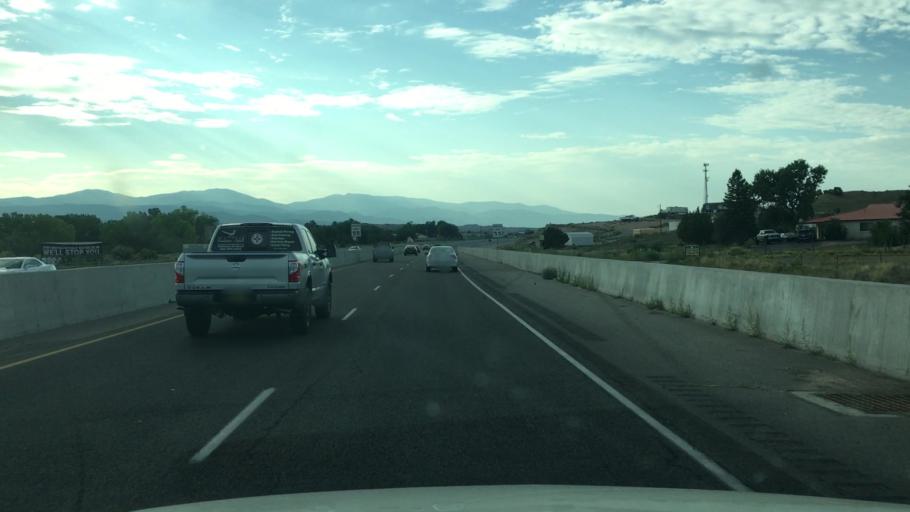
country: US
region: New Mexico
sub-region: Santa Fe County
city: El Valle de Arroyo Seco
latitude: 35.9603
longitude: -106.0267
